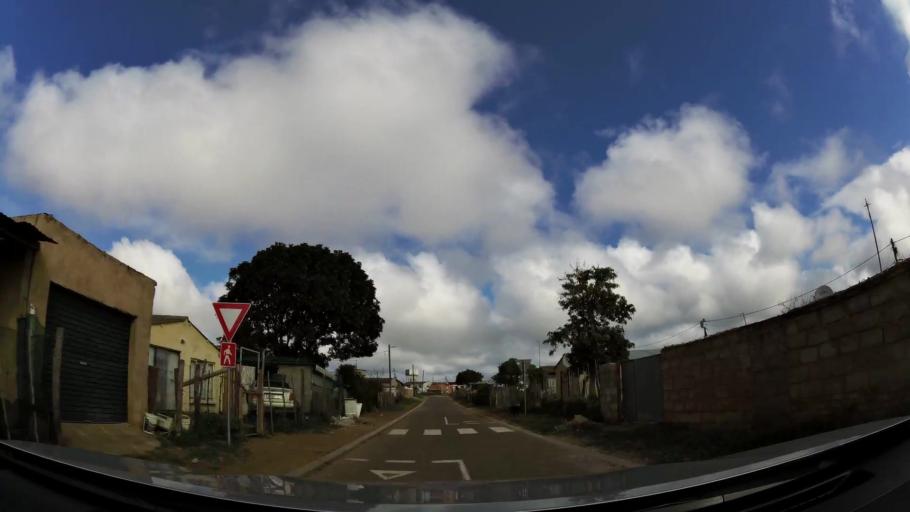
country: ZA
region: Western Cape
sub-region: Eden District Municipality
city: Plettenberg Bay
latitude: -34.0510
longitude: 23.3227
